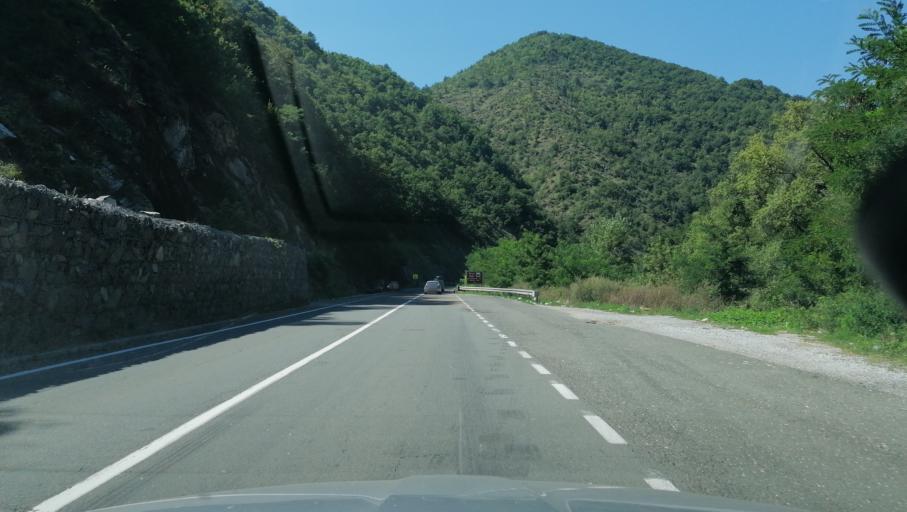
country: RS
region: Central Serbia
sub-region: Raski Okrug
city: Kraljevo
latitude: 43.5960
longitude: 20.5600
